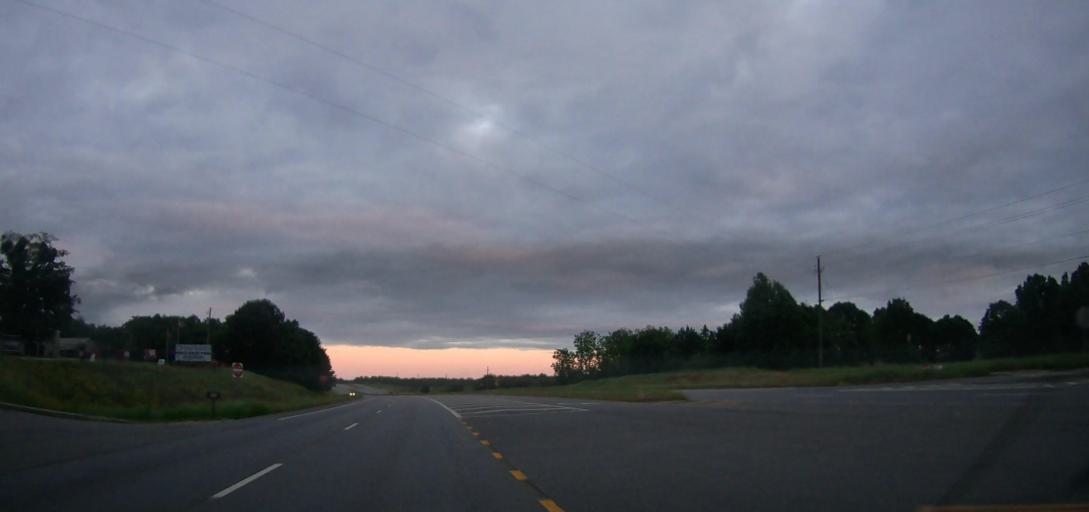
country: US
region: Georgia
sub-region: Jackson County
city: Arcade
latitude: 34.0644
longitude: -83.5337
